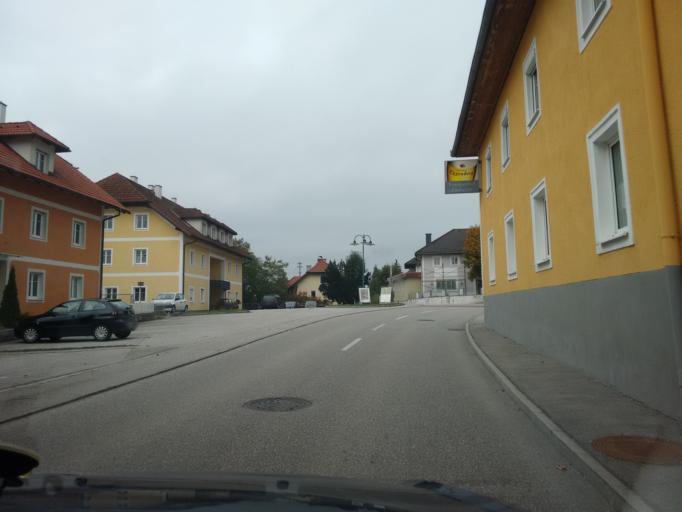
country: AT
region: Upper Austria
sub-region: Wels-Land
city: Sattledt
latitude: 48.0246
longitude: 14.0723
